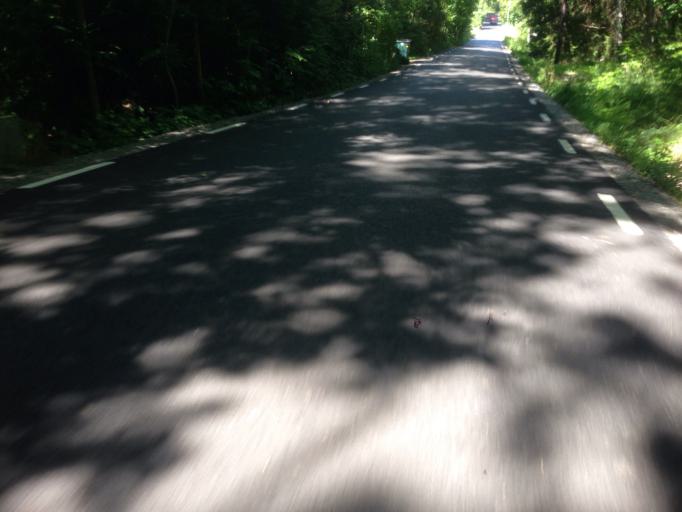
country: SE
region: Stockholm
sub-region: Vaxholms Kommun
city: Vaxholm
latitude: 59.3809
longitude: 18.3746
